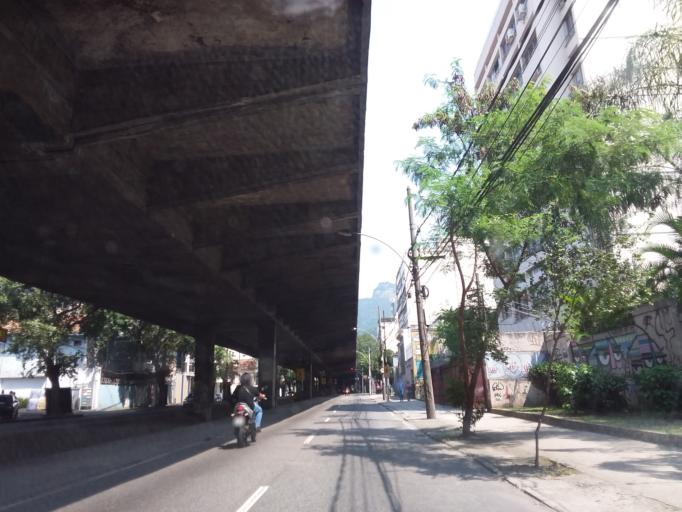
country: BR
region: Rio de Janeiro
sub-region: Rio De Janeiro
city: Rio de Janeiro
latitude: -22.9203
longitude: -43.2101
